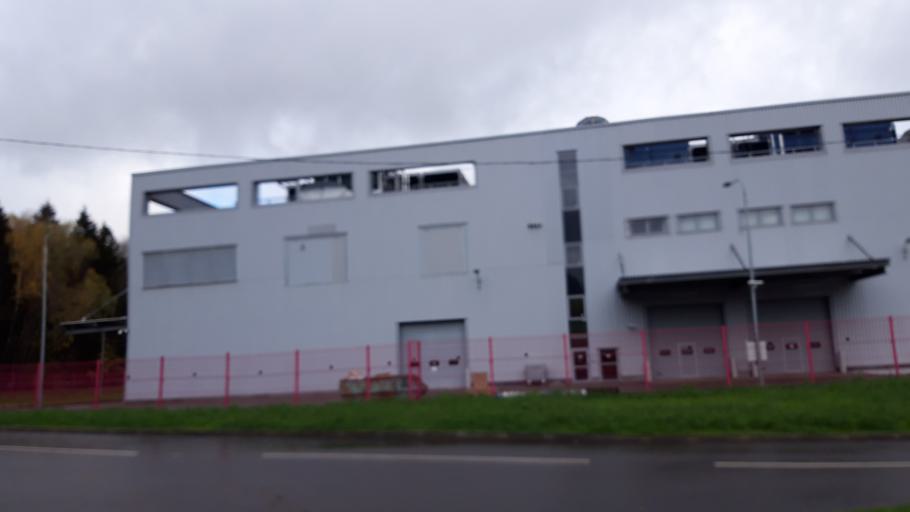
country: RU
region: Moscow
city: Zelenograd
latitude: 55.9773
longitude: 37.2137
